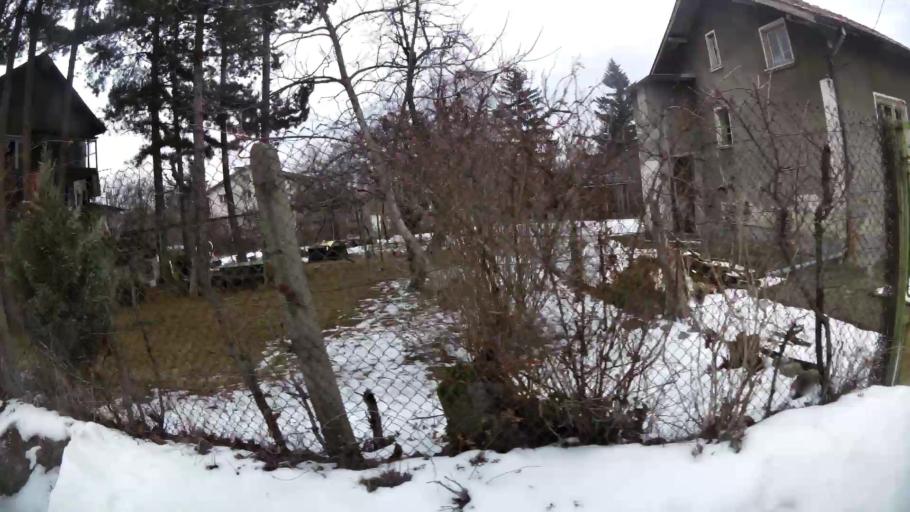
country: BG
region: Sofiya
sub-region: Obshtina Bozhurishte
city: Bozhurishte
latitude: 42.6728
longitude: 23.2349
